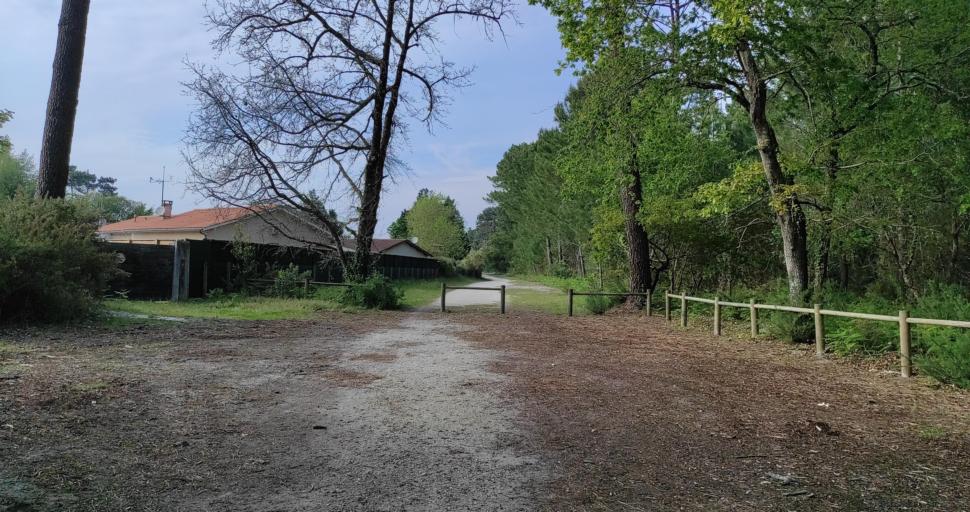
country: FR
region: Aquitaine
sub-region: Departement de la Gironde
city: Ares
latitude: 44.7533
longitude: -1.1265
